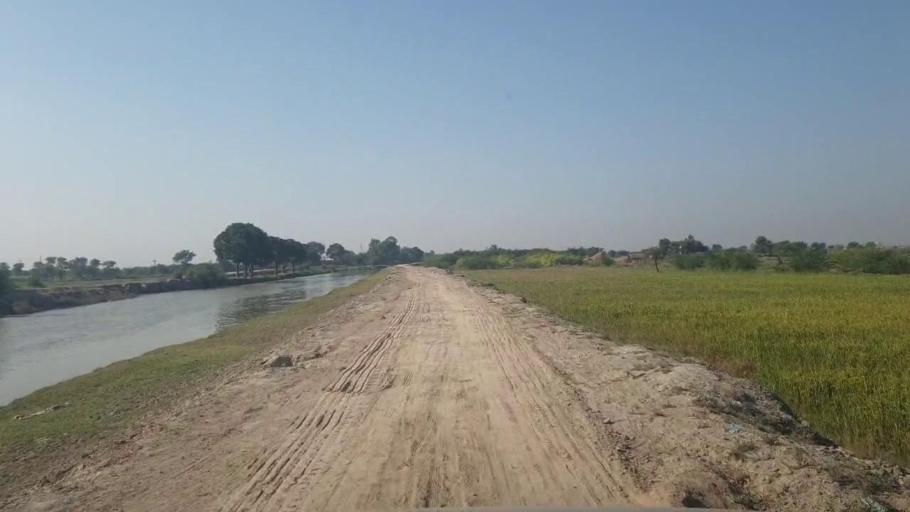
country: PK
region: Sindh
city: Badin
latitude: 24.6816
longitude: 68.8585
